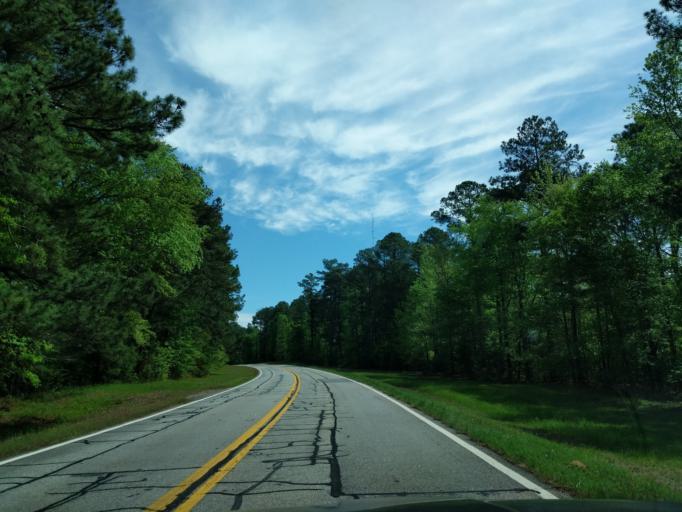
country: US
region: Georgia
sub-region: Columbia County
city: Appling
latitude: 33.6120
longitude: -82.3030
